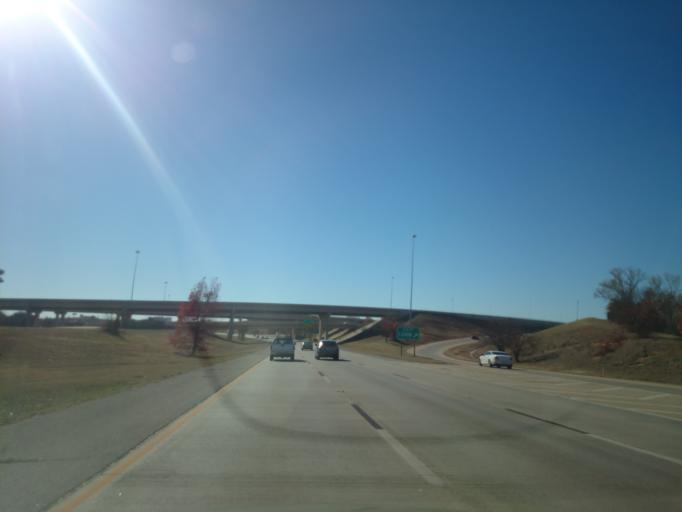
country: US
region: Oklahoma
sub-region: Oklahoma County
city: Edmond
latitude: 35.6031
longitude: -97.4291
